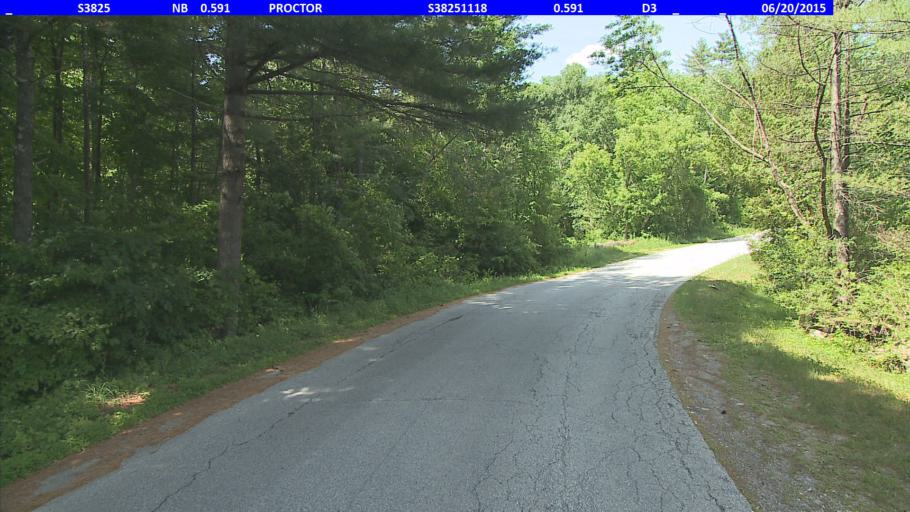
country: US
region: Vermont
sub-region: Rutland County
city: West Rutland
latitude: 43.6669
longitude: -73.0478
